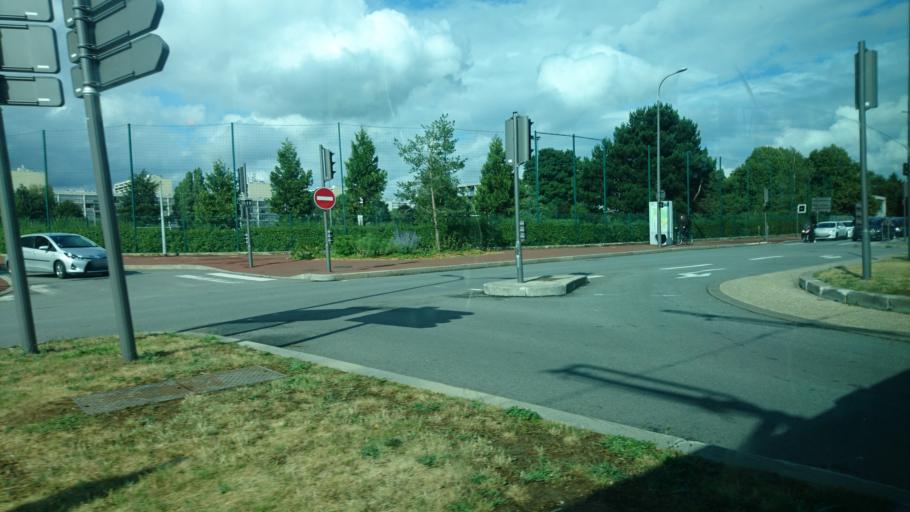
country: FR
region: Ile-de-France
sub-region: Departement des Yvelines
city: Velizy-Villacoublay
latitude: 48.7818
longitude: 2.1815
